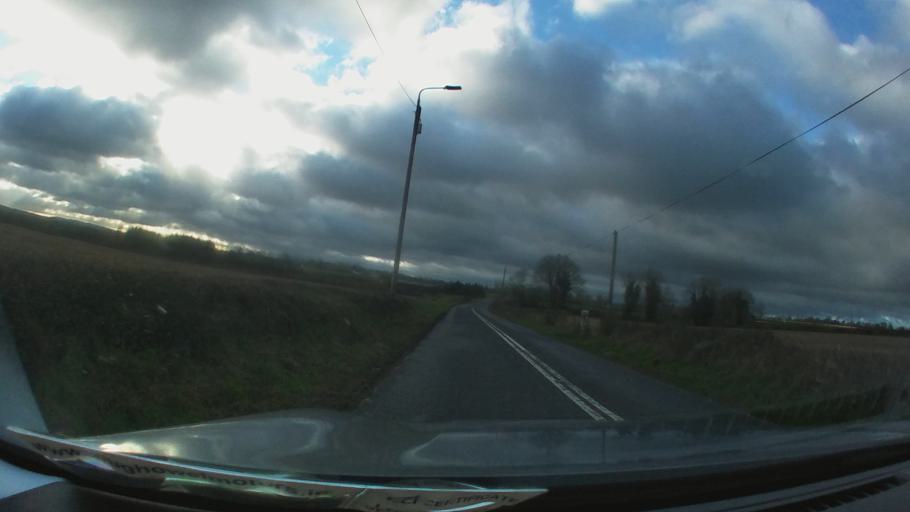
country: IE
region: Leinster
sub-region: Kilkenny
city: Thomastown
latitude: 52.5857
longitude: -7.0977
